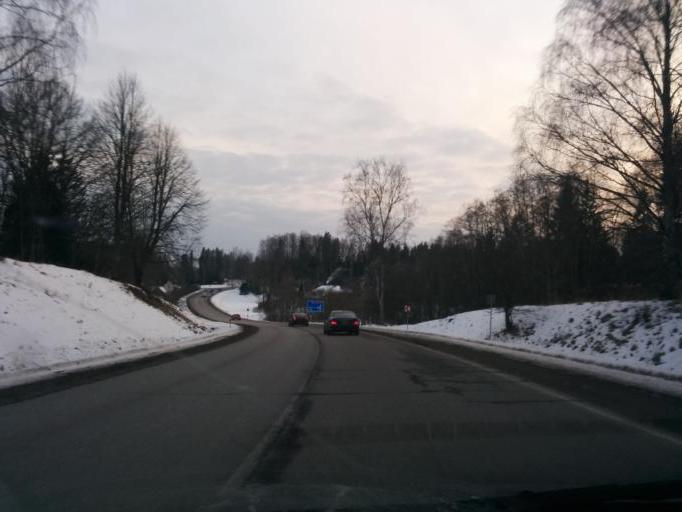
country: LV
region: Amatas Novads
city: Drabesi
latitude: 57.2357
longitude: 25.2746
